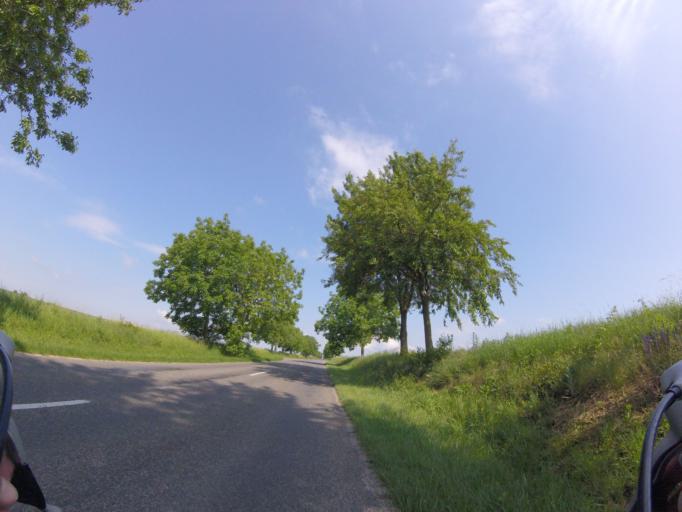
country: HU
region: Baranya
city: Kozarmisleny
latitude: 45.9770
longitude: 18.3387
